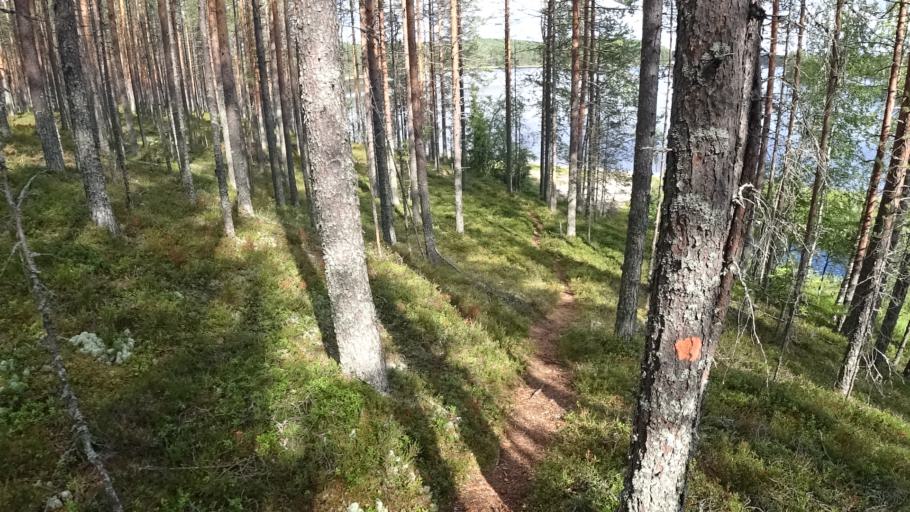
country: FI
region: North Karelia
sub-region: Joensuu
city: Ilomantsi
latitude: 62.6068
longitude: 31.1891
